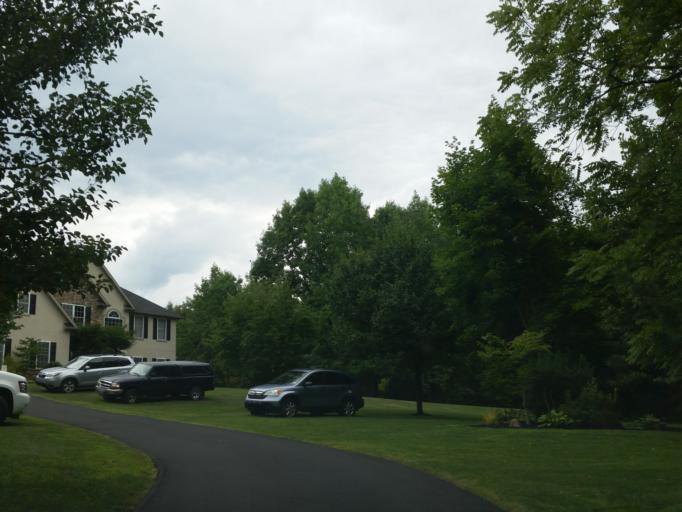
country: US
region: Pennsylvania
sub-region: Berks County
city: Alleghenyville
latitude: 40.2290
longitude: -75.9593
